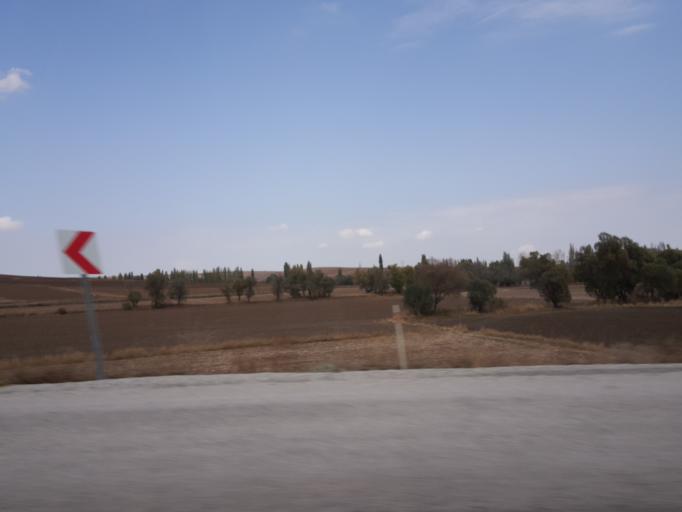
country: TR
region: Corum
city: Alaca
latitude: 40.1552
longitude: 34.7575
